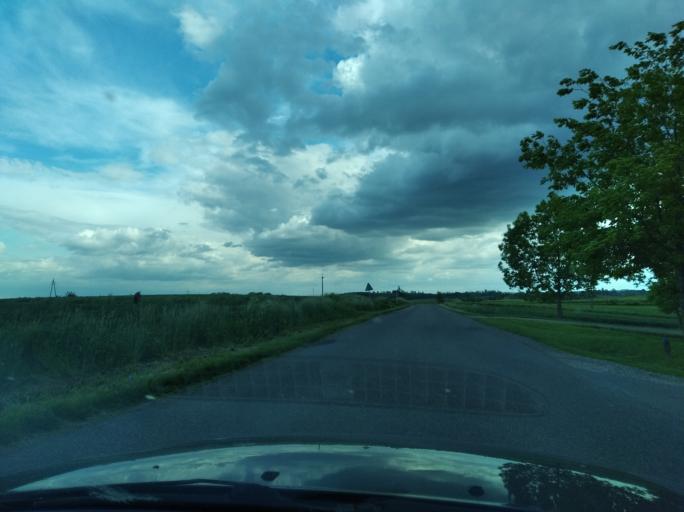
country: PL
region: Subcarpathian Voivodeship
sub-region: Powiat jaroslawski
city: Pawlosiow
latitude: 49.9516
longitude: 22.6663
